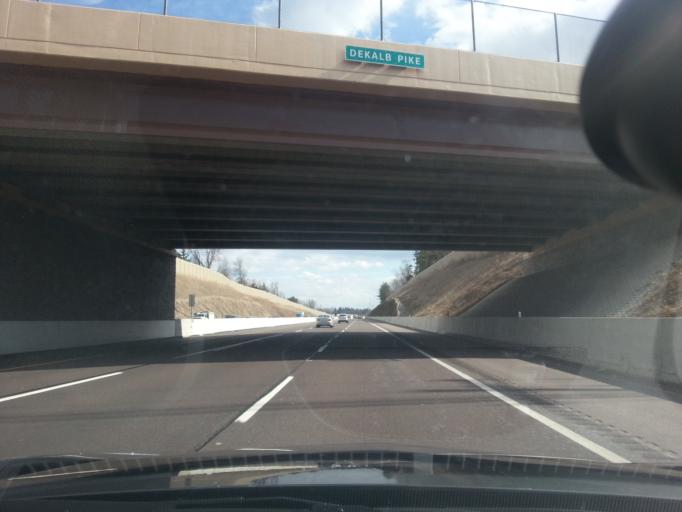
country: US
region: Pennsylvania
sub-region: Montgomery County
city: Blue Bell
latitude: 40.1597
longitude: -75.2985
